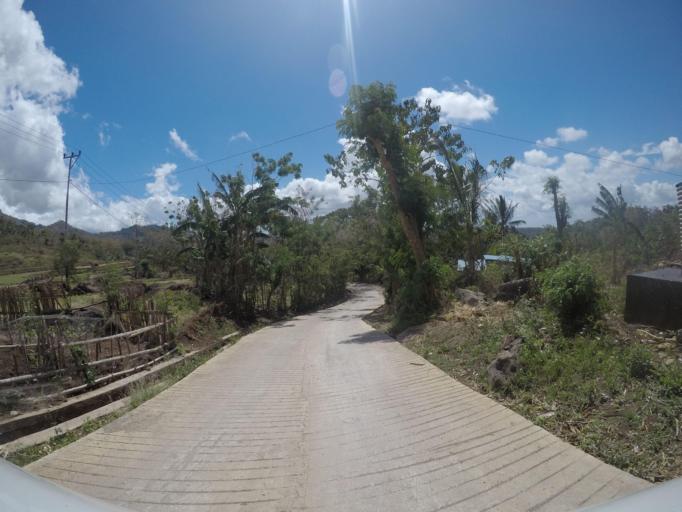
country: TL
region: Lautem
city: Lospalos
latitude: -8.5367
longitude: 126.8002
